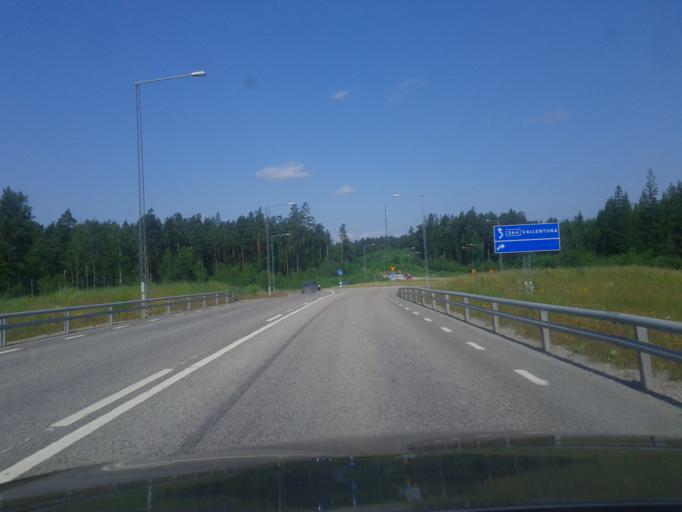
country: SE
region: Stockholm
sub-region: Vallentuna Kommun
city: Vallentuna
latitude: 59.4892
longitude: 18.1092
